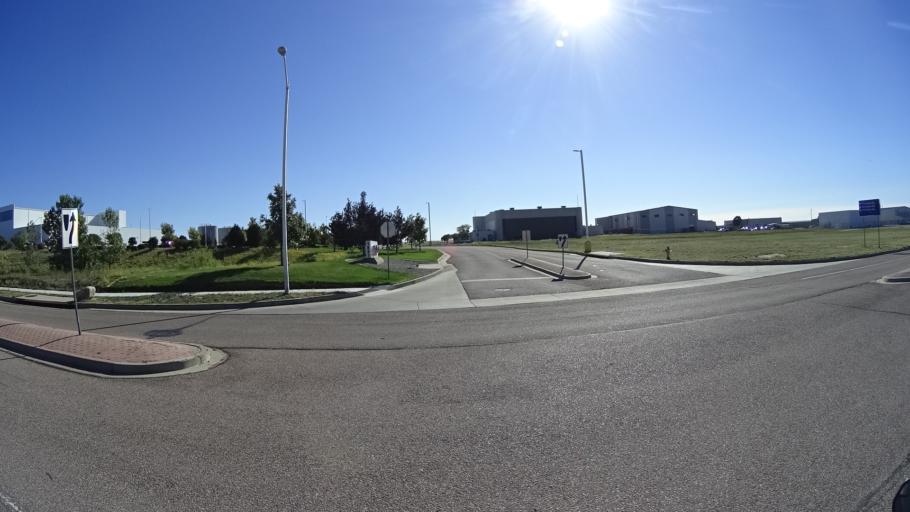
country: US
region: Colorado
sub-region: El Paso County
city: Security-Widefield
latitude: 38.8034
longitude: -104.7237
